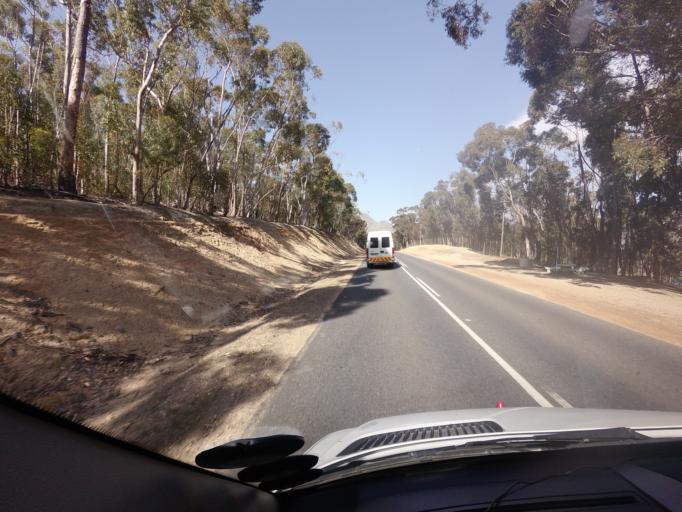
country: ZA
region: Western Cape
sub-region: Overberg District Municipality
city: Hermanus
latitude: -34.4048
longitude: 19.3651
